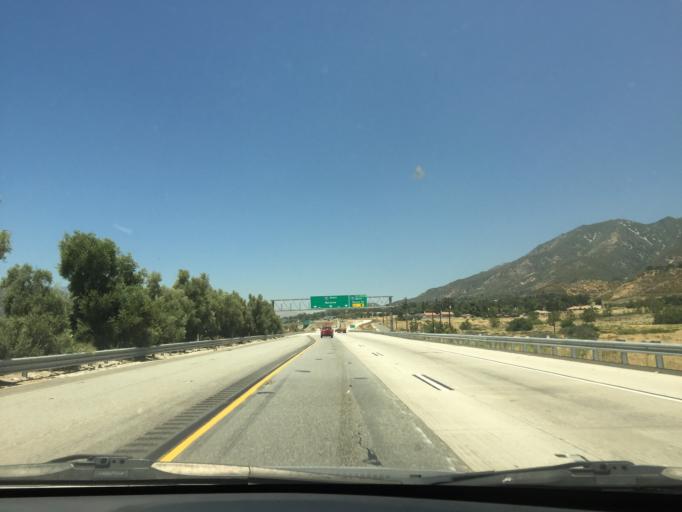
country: US
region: California
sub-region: San Bernardino County
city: Muscoy
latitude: 34.2177
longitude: -117.3957
